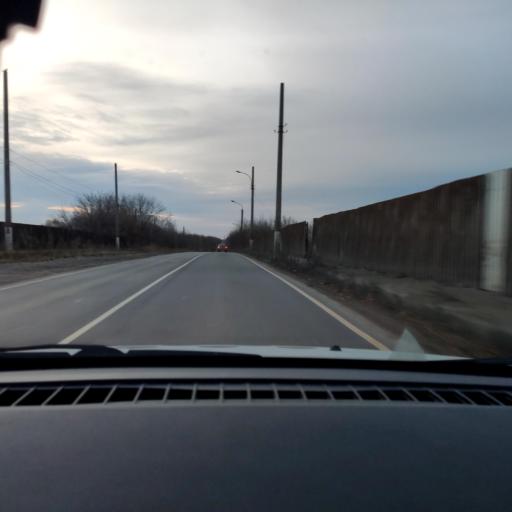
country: RU
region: Perm
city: Gamovo
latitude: 57.9105
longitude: 56.1612
